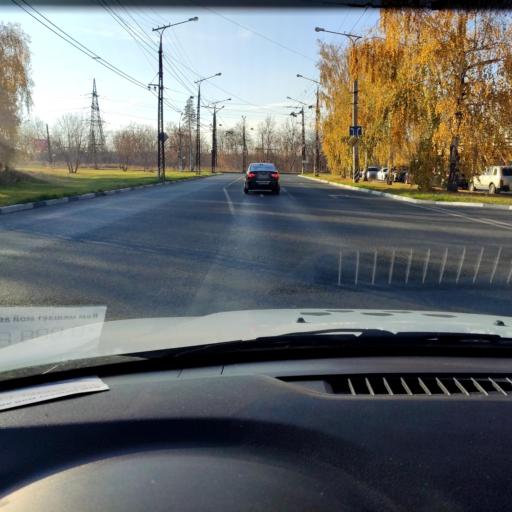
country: RU
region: Samara
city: Tol'yatti
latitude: 53.4988
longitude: 49.3905
